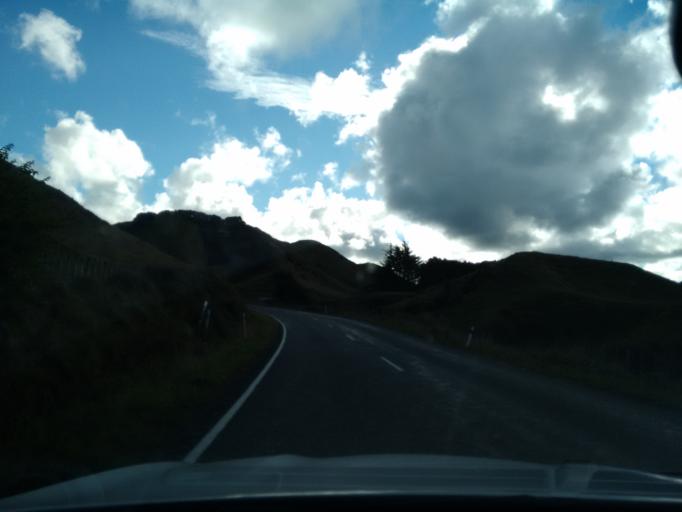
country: NZ
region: Manawatu-Wanganui
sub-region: Ruapehu District
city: Waiouru
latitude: -39.4261
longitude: 175.2569
